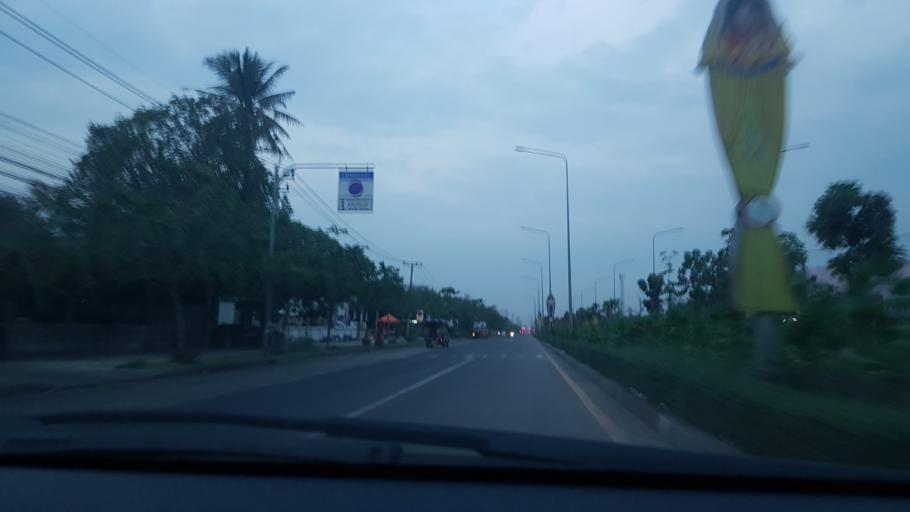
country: TH
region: Bangkok
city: Nong Khaem
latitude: 13.7133
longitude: 100.3639
